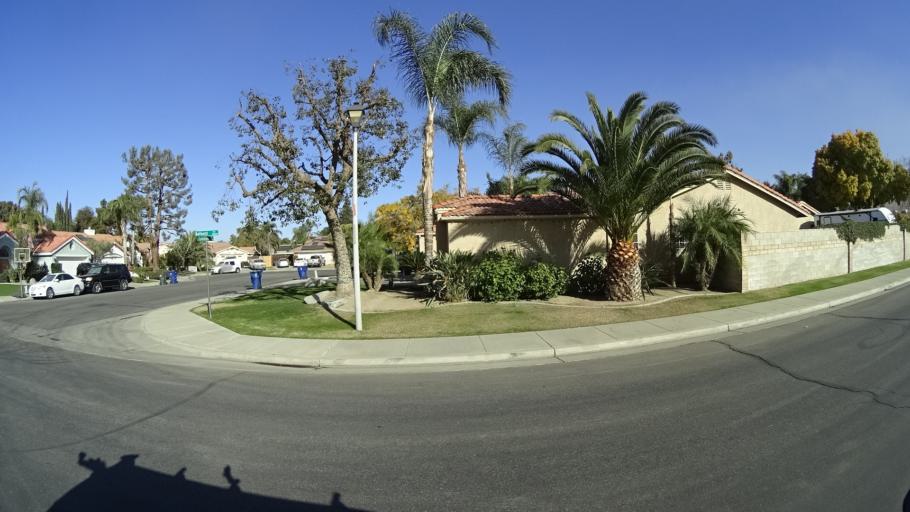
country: US
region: California
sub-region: Kern County
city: Greenfield
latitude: 35.2768
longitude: -119.0414
